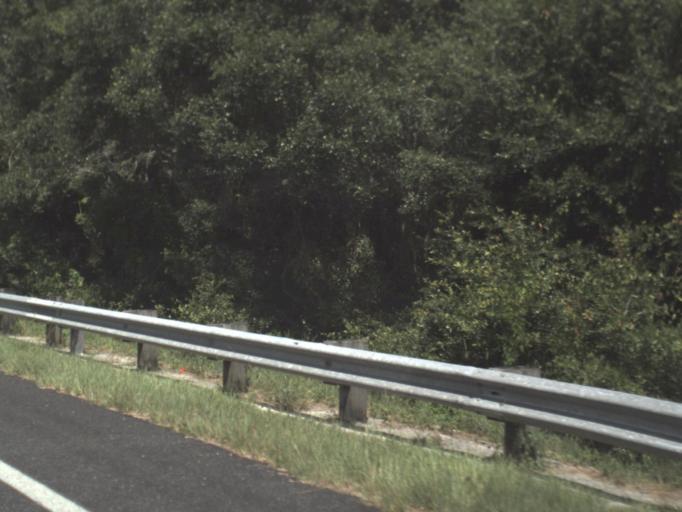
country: US
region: Florida
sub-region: Levy County
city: Manatee Road
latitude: 29.5902
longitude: -82.9434
